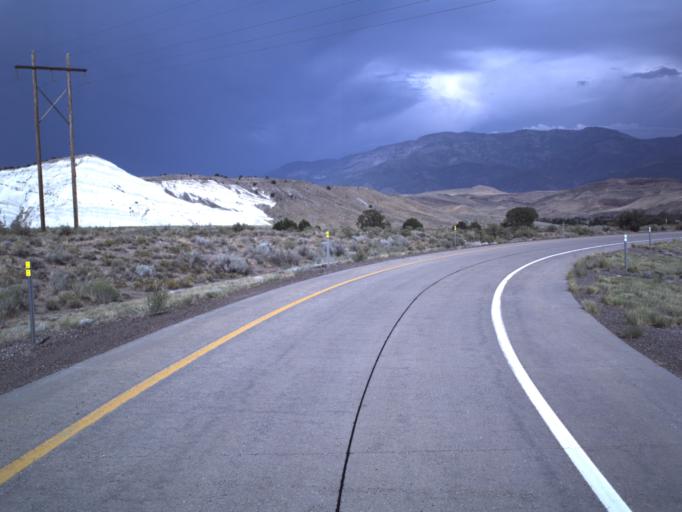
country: US
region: Utah
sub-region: Sevier County
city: Monroe
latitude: 38.6025
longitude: -112.2535
